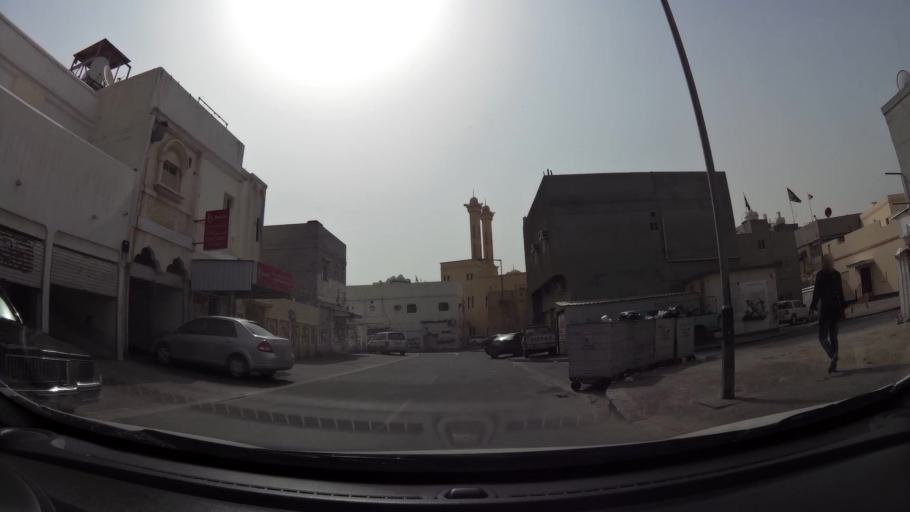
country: BH
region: Manama
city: Jidd Hafs
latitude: 26.2314
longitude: 50.5281
